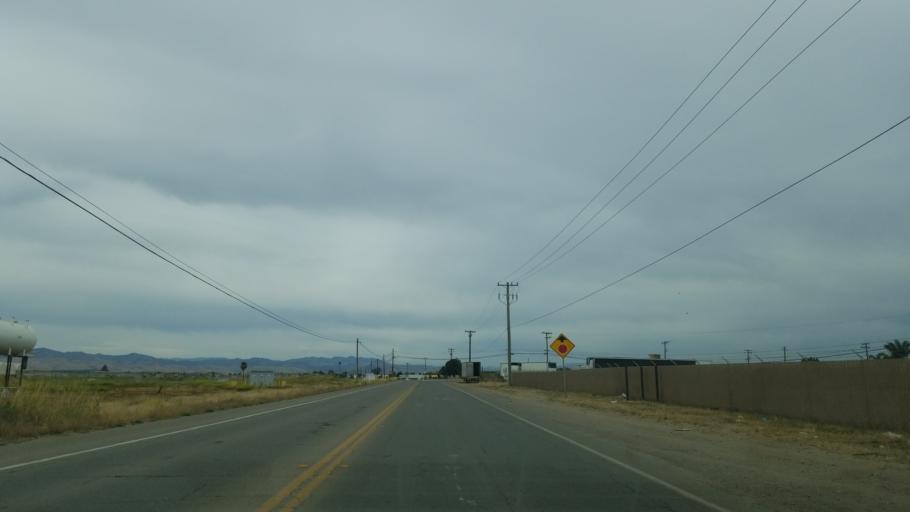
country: US
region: California
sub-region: Santa Barbara County
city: Santa Maria
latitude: 34.9212
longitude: -120.4769
